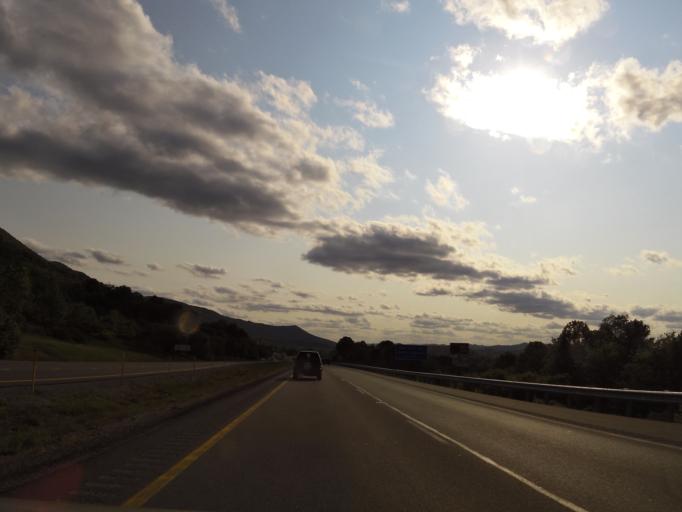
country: US
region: West Virginia
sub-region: Mercer County
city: Bluefield
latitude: 37.2471
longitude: -81.2147
